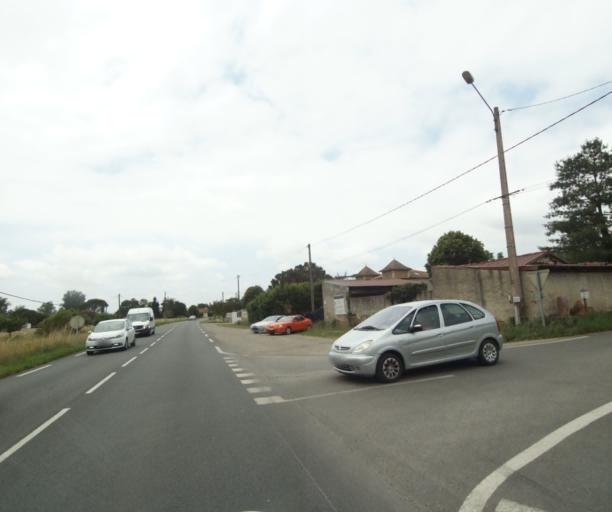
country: FR
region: Midi-Pyrenees
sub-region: Departement du Tarn-et-Garonne
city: Montauban
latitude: 43.9929
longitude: 1.3883
